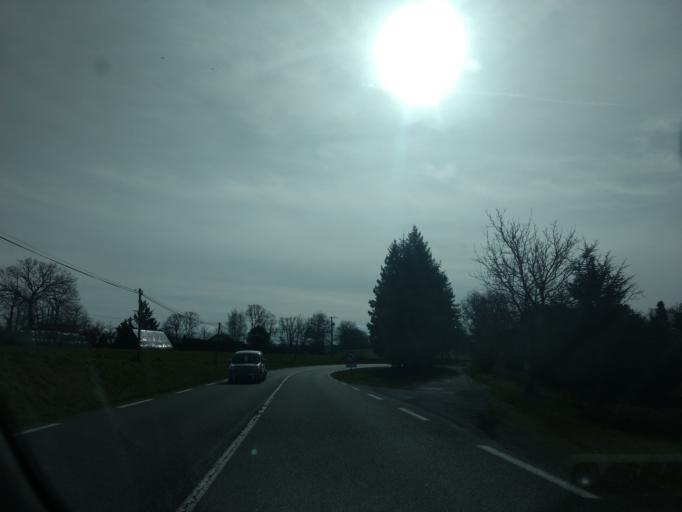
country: FR
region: Midi-Pyrenees
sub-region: Departement de l'Aveyron
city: Villeneuve
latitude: 44.4094
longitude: 2.0965
